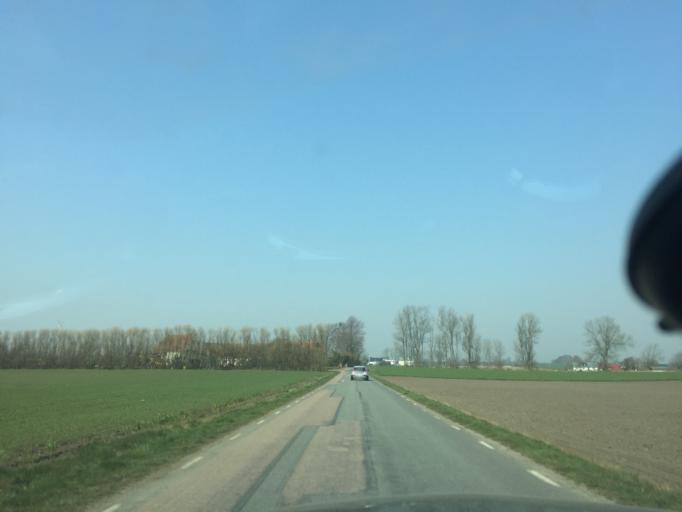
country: SE
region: Skane
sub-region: Simrishamns Kommun
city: Simrishamn
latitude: 55.4634
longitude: 14.2092
